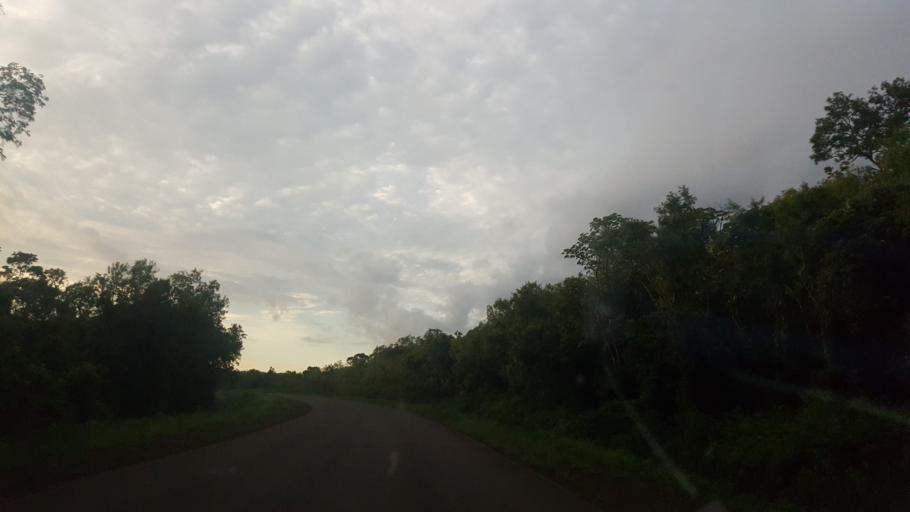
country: AR
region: Misiones
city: Dos de Mayo
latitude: -26.9187
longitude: -54.7321
